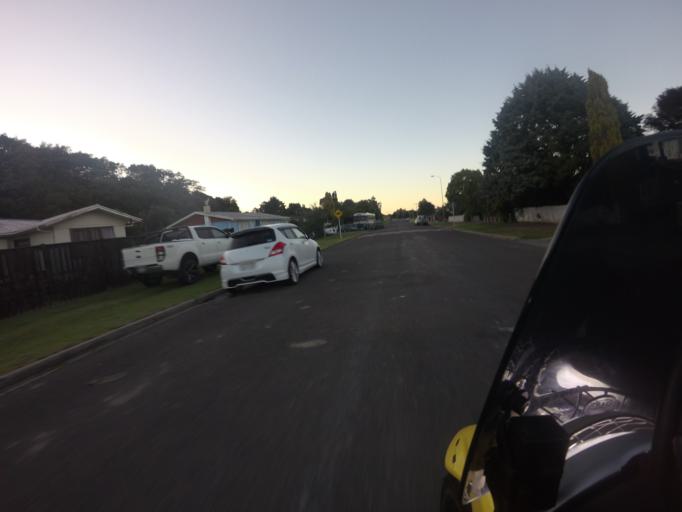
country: NZ
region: Gisborne
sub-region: Gisborne District
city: Gisborne
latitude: -38.6814
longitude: 178.0555
